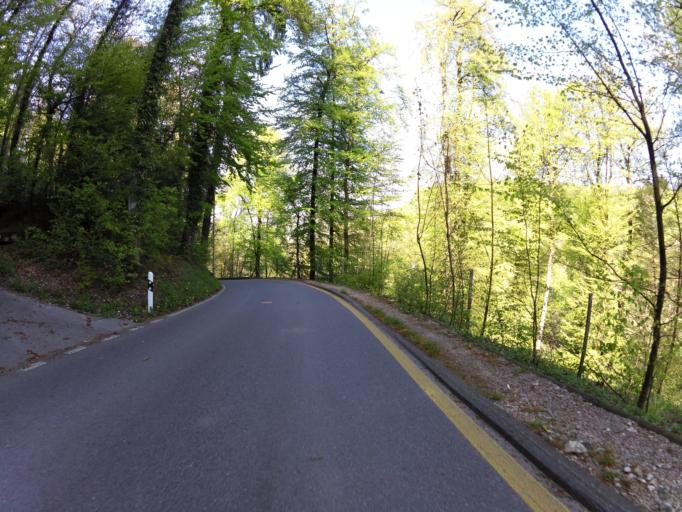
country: CH
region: Aargau
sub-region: Bezirk Aarau
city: Aarau
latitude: 47.3802
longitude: 8.0289
